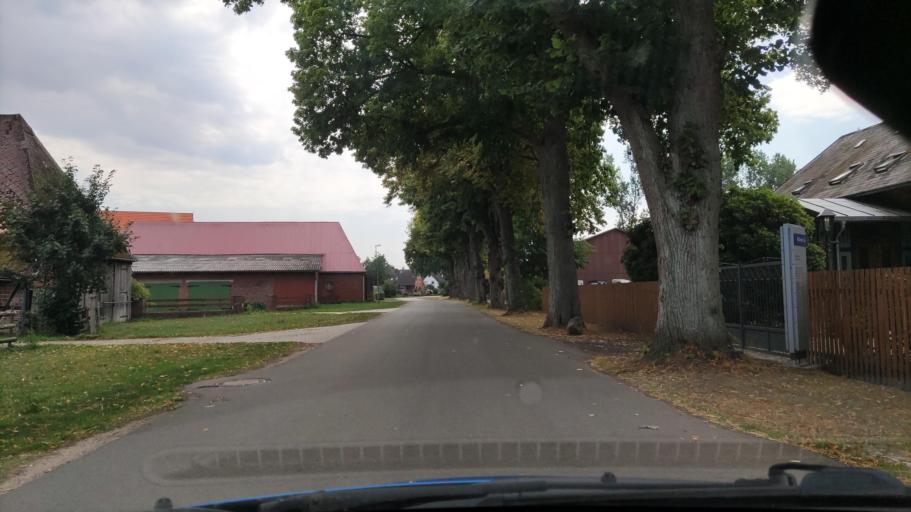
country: DE
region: Lower Saxony
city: Wittorf
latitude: 53.3338
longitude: 10.3784
